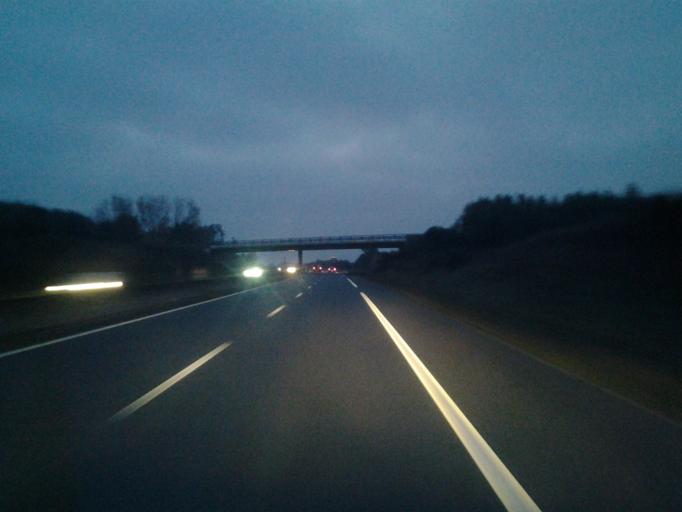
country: FR
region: Pays de la Loire
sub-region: Departement de la Vendee
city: Les Clouzeaux
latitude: 46.6382
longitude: -1.4965
